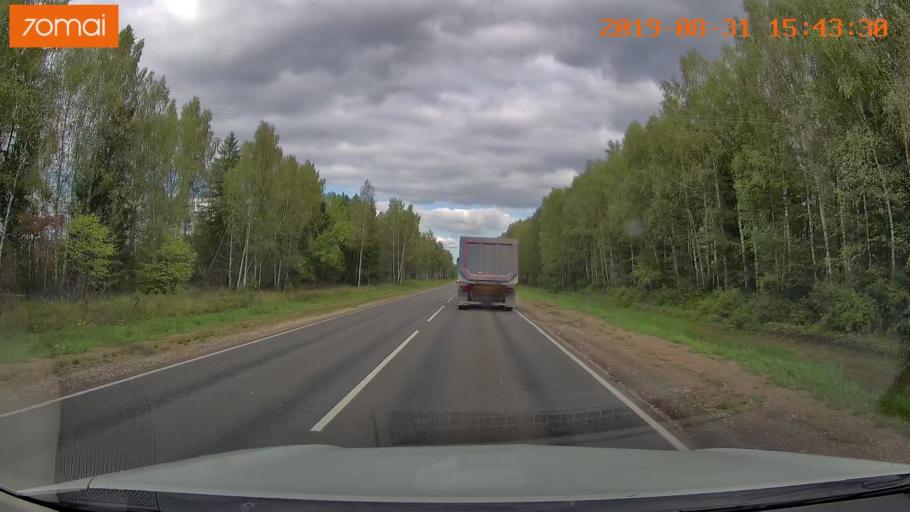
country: RU
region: Kaluga
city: Mosal'sk
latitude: 54.6533
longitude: 34.9118
